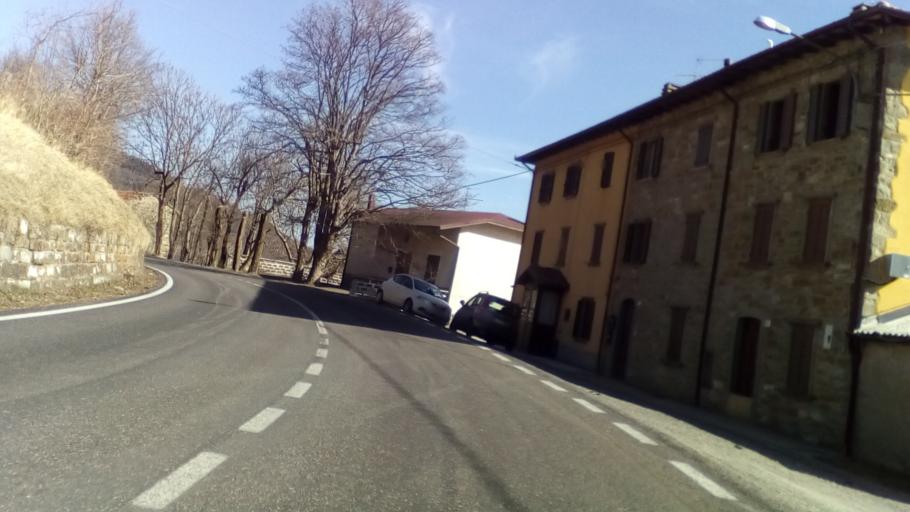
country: IT
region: Emilia-Romagna
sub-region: Provincia di Modena
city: Riolunato
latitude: 44.2656
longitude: 10.6670
